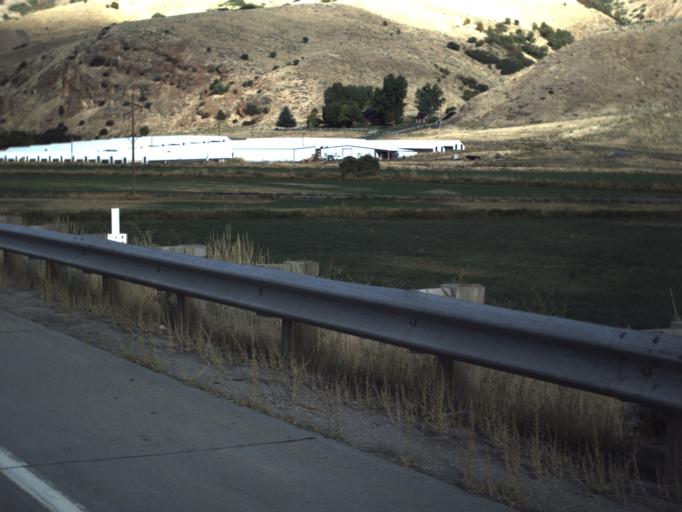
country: US
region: Utah
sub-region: Morgan County
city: Morgan
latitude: 41.0519
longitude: -111.6254
